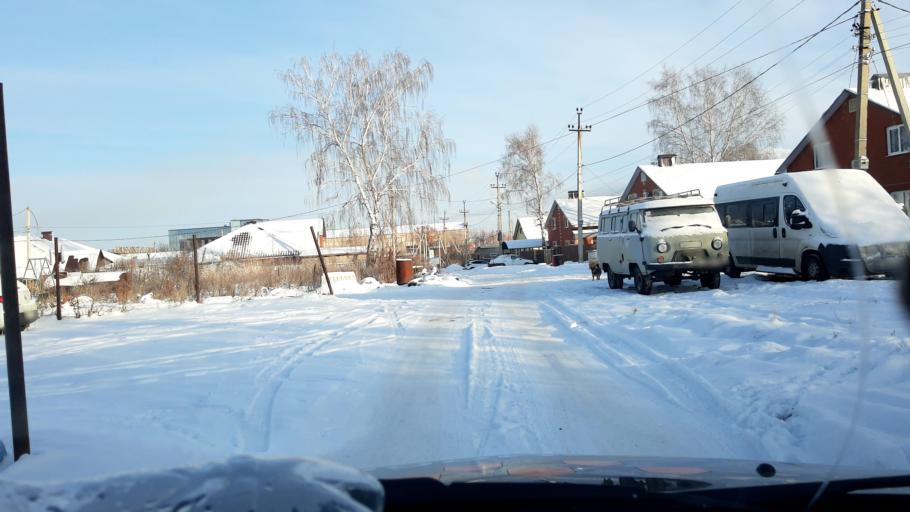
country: RU
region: Bashkortostan
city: Avdon
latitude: 54.6875
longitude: 55.7898
